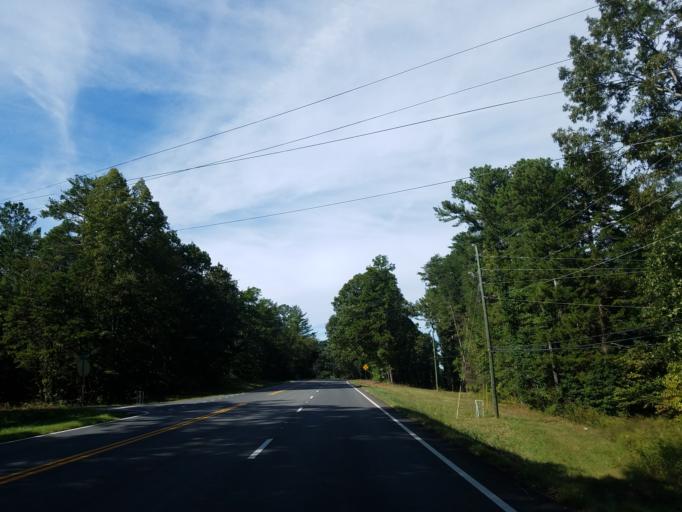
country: US
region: Georgia
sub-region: Pickens County
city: Nelson
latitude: 34.4232
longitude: -84.3947
